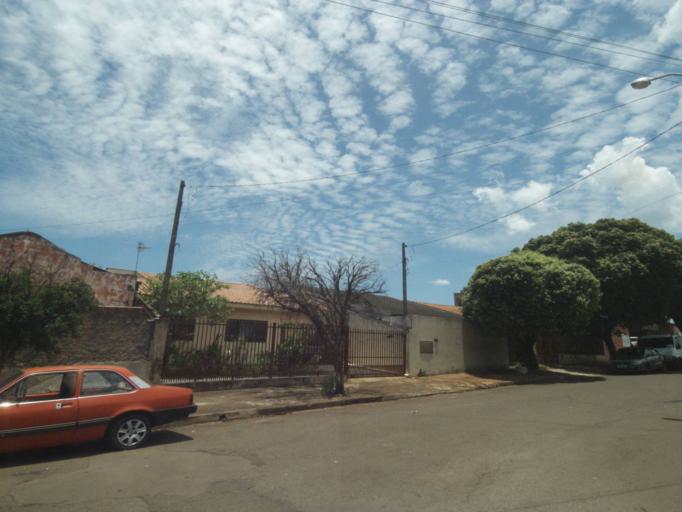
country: BR
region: Parana
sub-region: Londrina
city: Londrina
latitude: -23.3660
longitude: -51.1424
